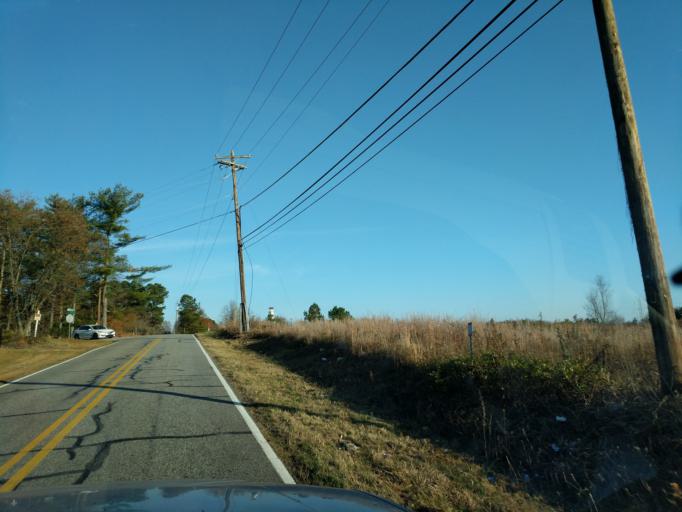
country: US
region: South Carolina
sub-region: Spartanburg County
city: Valley Falls
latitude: 35.0146
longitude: -81.9437
